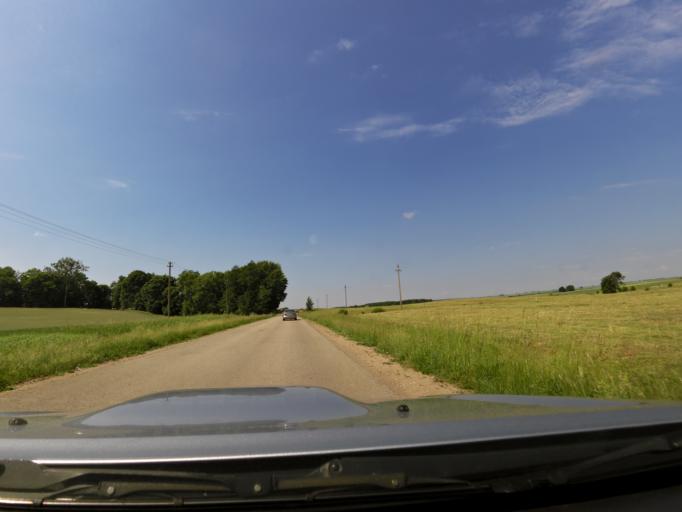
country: LT
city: Vilkaviskis
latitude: 54.5043
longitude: 23.0102
